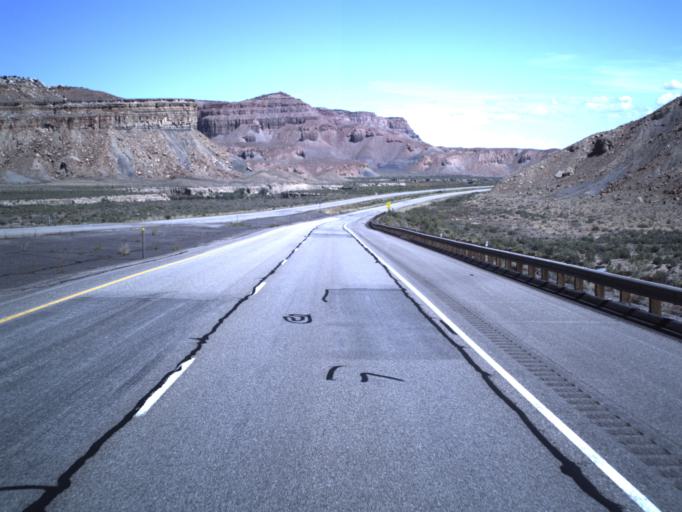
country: US
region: Utah
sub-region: Emery County
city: Ferron
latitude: 38.8069
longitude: -111.2592
